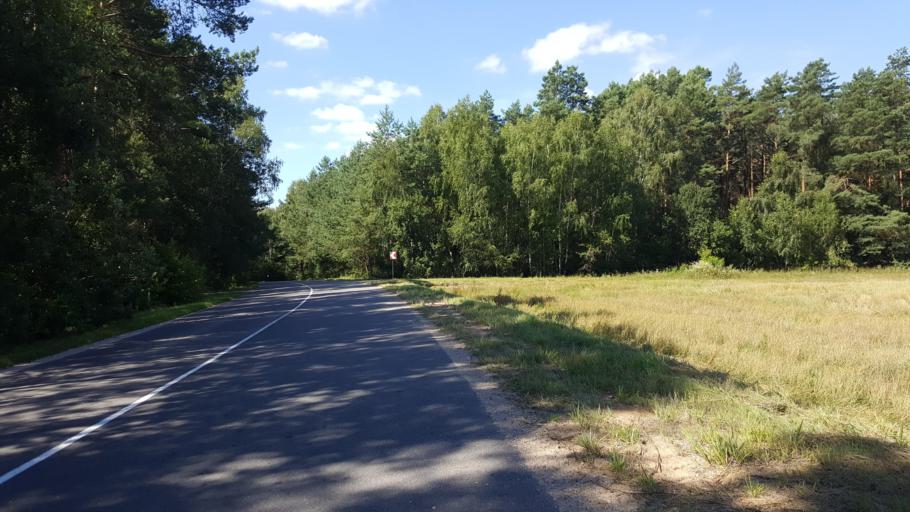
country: BY
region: Brest
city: Kamyanyets
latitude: 52.3827
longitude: 23.6978
